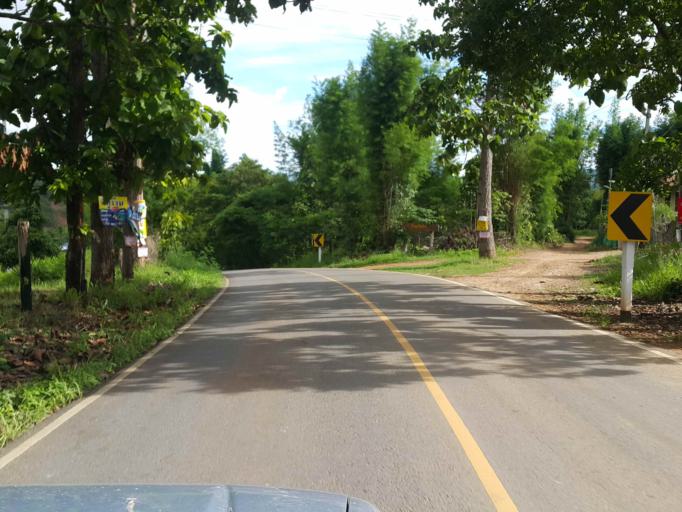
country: TH
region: Chiang Mai
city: Mae Chaem
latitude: 18.4892
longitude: 98.3830
